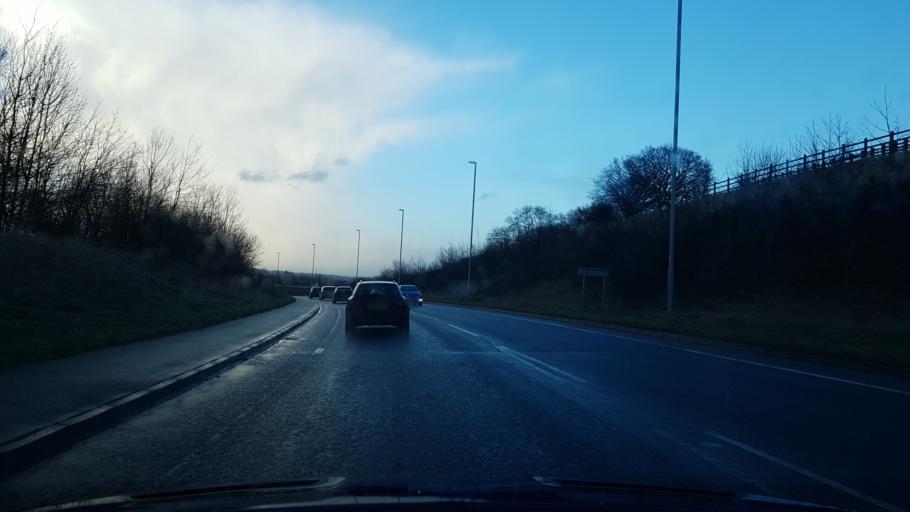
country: GB
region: England
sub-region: City and Borough of Wakefield
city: Castleford
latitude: 53.7037
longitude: -1.3697
